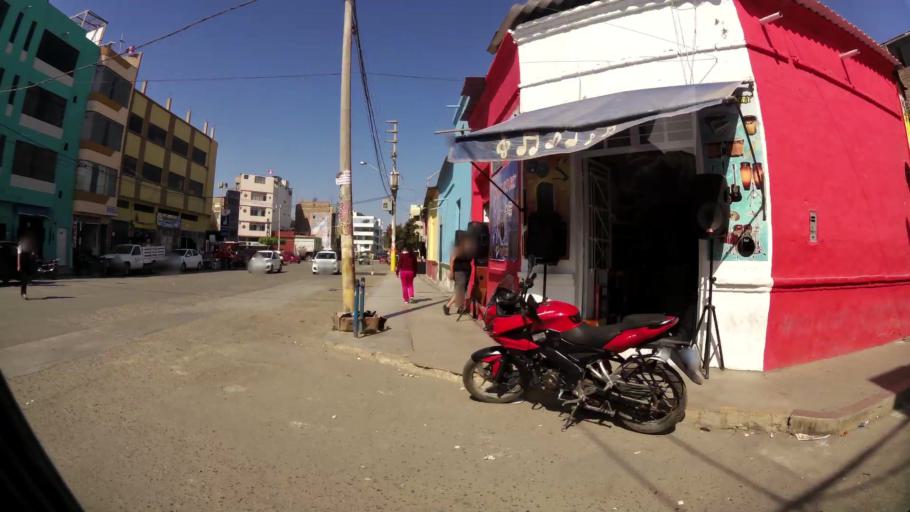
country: PE
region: Lambayeque
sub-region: Provincia de Chiclayo
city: Santa Rosa
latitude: -6.7680
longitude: -79.8369
